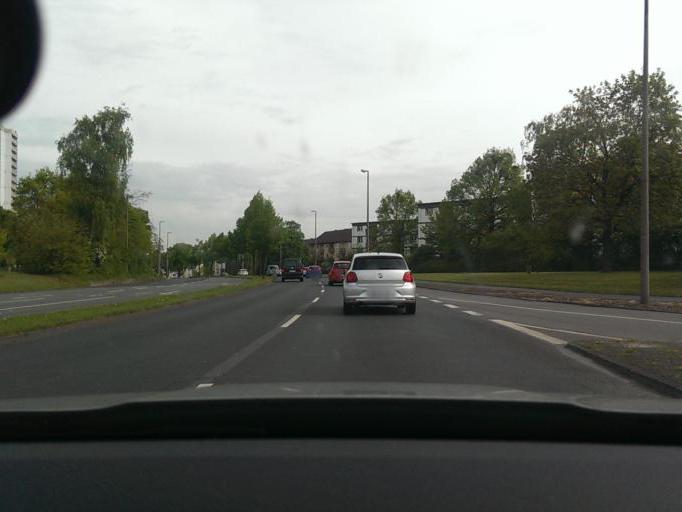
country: DE
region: Lower Saxony
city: Wolfsburg
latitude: 52.4194
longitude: 10.7998
